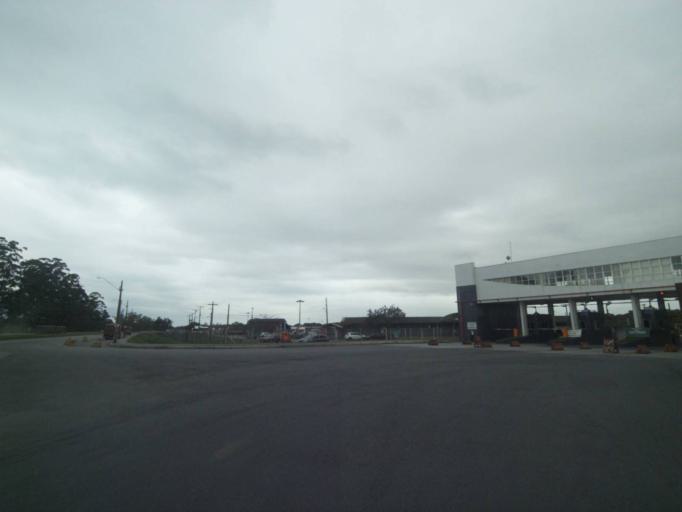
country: BR
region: Parana
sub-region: Paranagua
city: Paranagua
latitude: -25.5402
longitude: -48.5583
